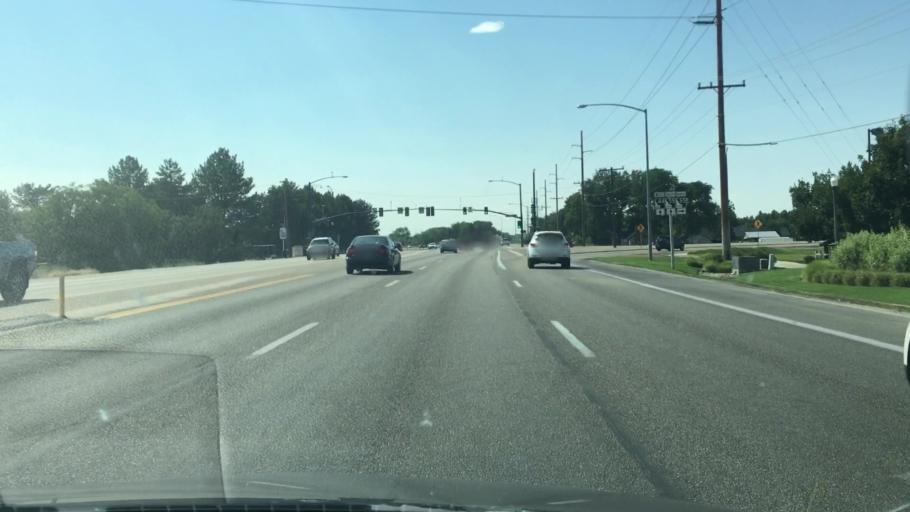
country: US
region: Idaho
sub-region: Ada County
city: Eagle
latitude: 43.6841
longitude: -116.3185
